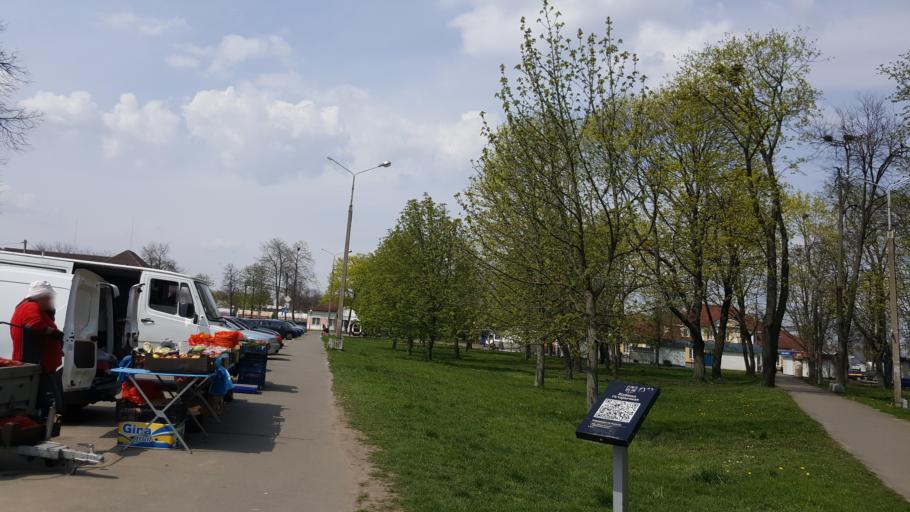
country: BY
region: Brest
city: Zhabinka
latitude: 52.1995
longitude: 24.0182
